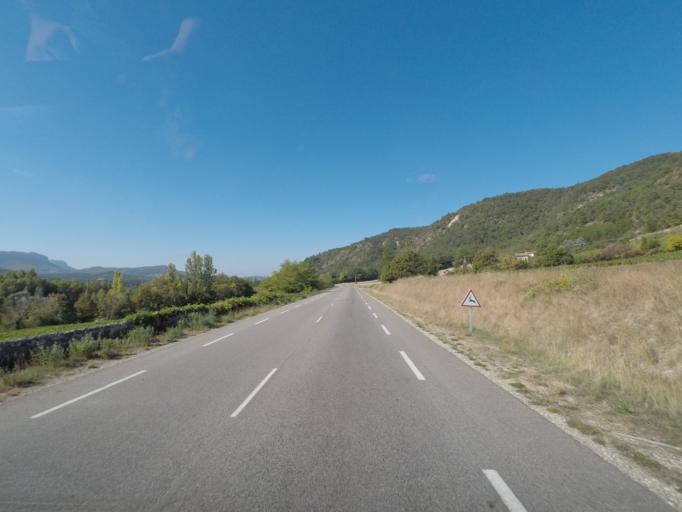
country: FR
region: Rhone-Alpes
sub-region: Departement de la Drome
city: Aouste-sur-Sye
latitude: 44.6977
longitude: 5.1567
